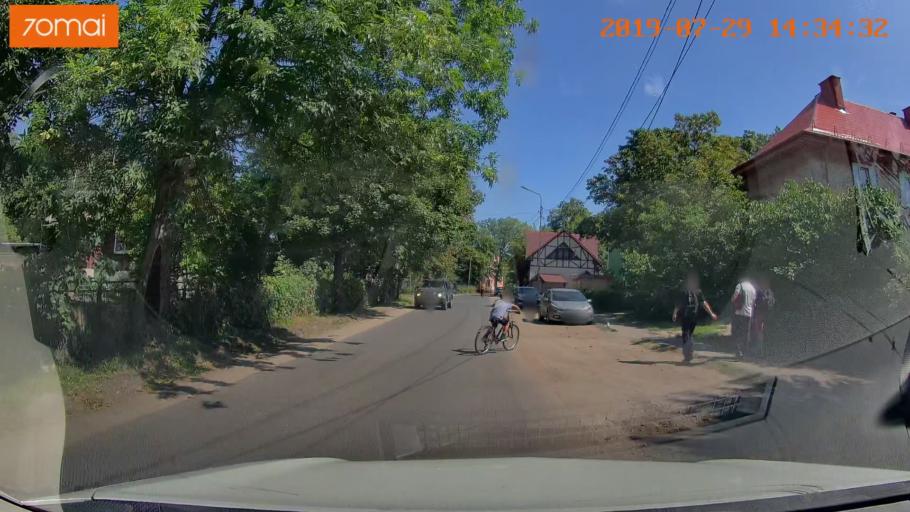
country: RU
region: Kaliningrad
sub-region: Gorod Kaliningrad
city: Baltiysk
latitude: 54.6459
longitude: 19.8884
